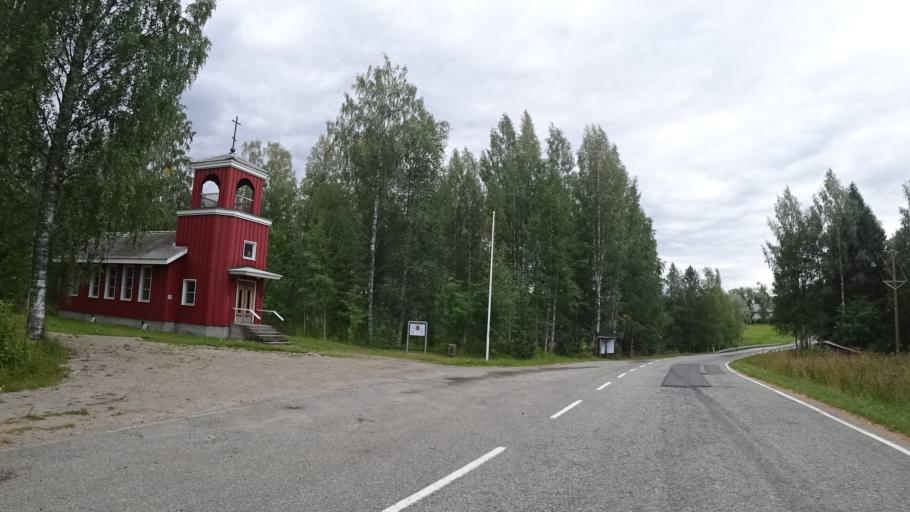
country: FI
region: North Karelia
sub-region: Joensuu
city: Ilomantsi
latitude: 62.4528
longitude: 31.1143
